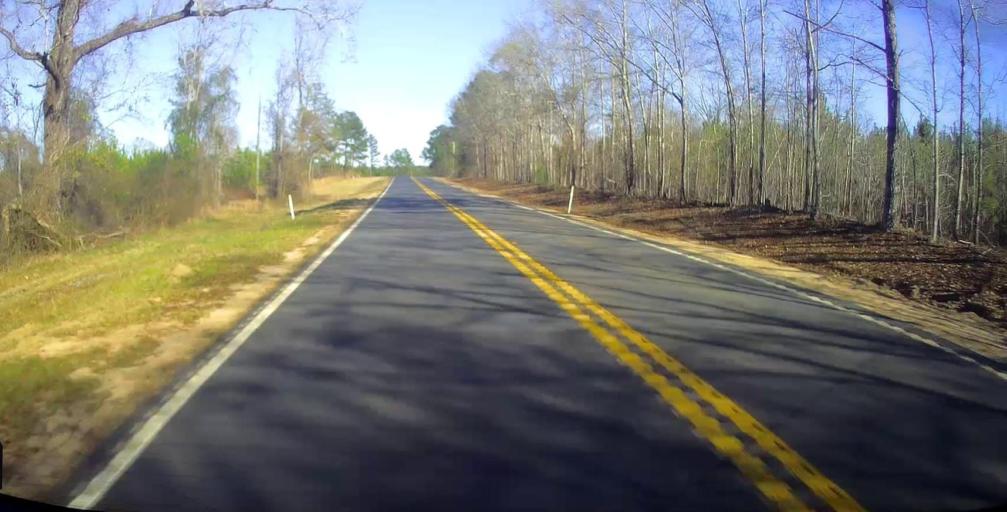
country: US
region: Georgia
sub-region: Taylor County
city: Butler
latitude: 32.6604
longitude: -84.3554
